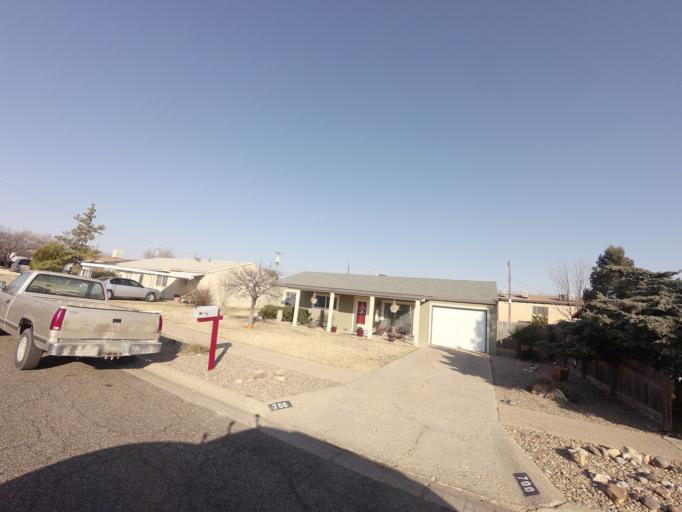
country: US
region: New Mexico
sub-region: Curry County
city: Clovis
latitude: 34.4184
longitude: -103.2126
